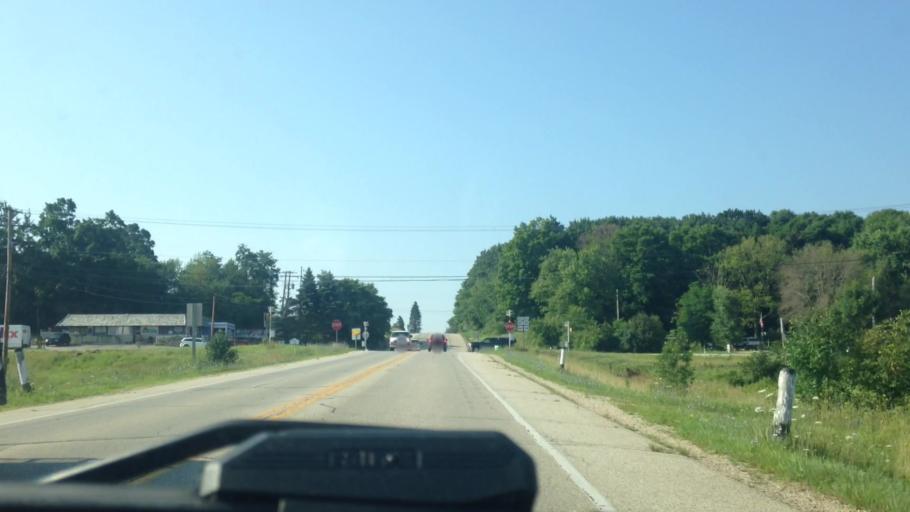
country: US
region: Wisconsin
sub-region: Washington County
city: Richfield
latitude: 43.2524
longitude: -88.2618
